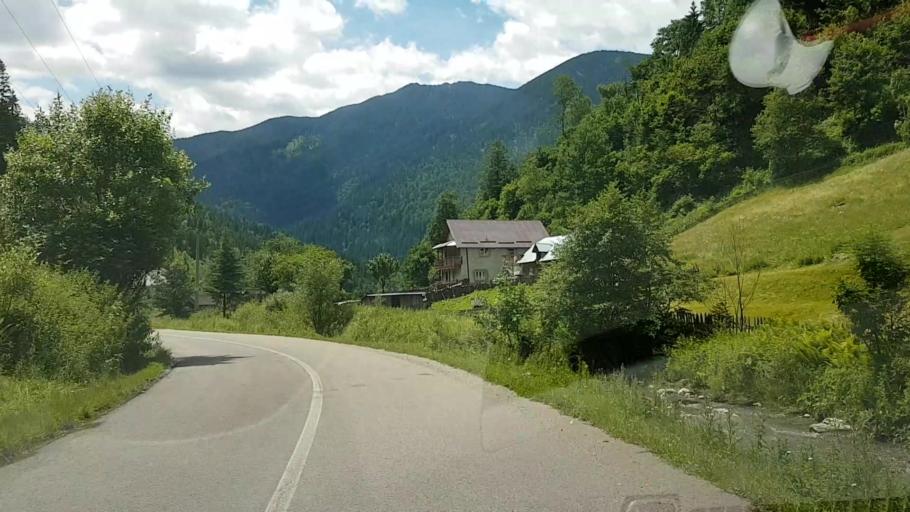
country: RO
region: Suceava
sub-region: Comuna Crucea
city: Crucea
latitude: 47.4057
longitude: 25.5749
